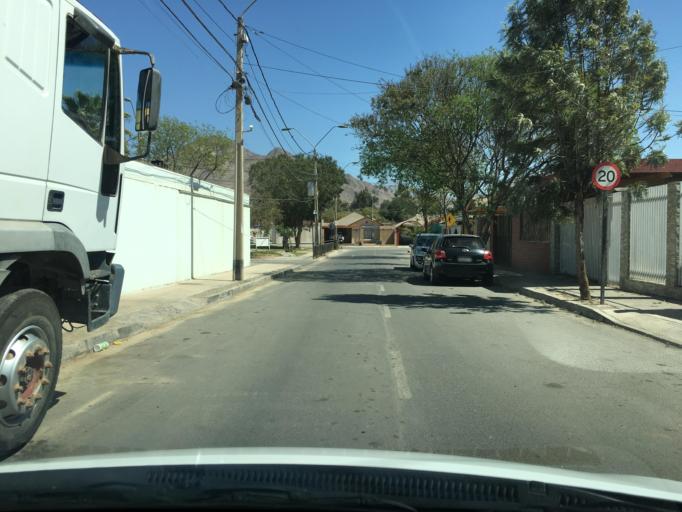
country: CL
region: Atacama
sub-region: Provincia de Copiapo
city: Copiapo
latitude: -27.4113
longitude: -70.2861
